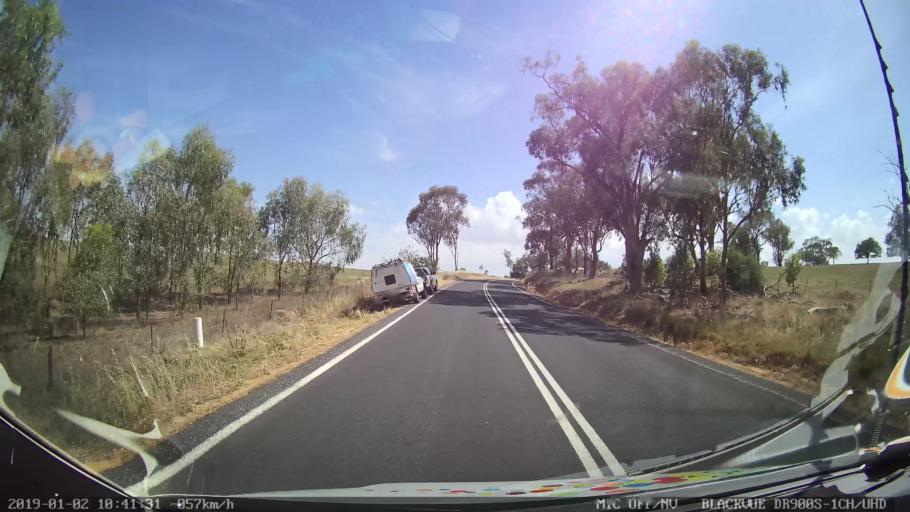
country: AU
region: New South Wales
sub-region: Cootamundra
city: Cootamundra
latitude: -34.7934
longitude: 148.3065
